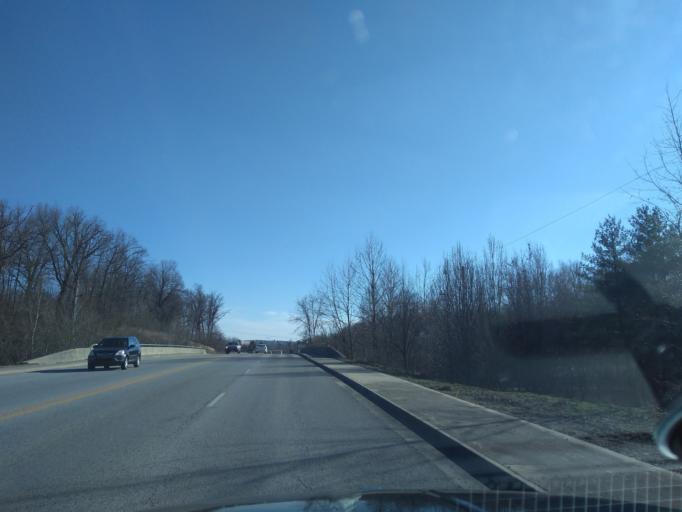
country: US
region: Arkansas
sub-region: Washington County
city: Johnson
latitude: 36.1286
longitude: -94.1631
